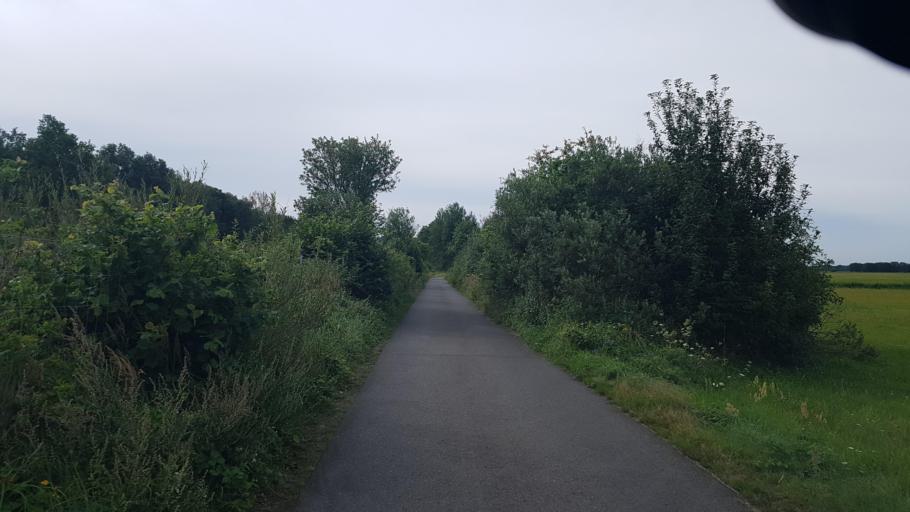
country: DE
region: Brandenburg
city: Bronkow
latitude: 51.6213
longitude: 13.9460
